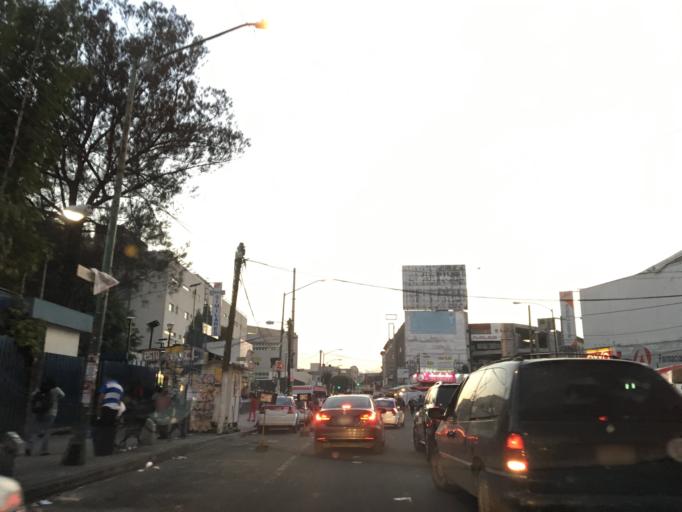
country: MX
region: Mexico City
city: Benito Juarez
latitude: 19.4140
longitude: -99.1528
